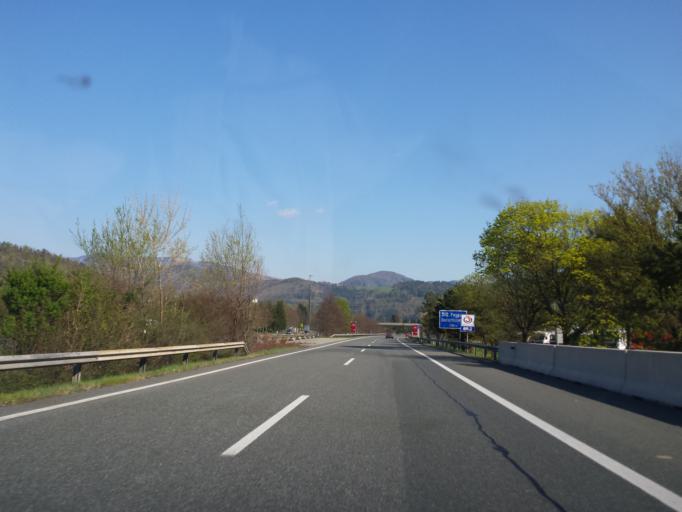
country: AT
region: Styria
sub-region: Politischer Bezirk Graz-Umgebung
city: Deutschfeistritz
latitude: 47.2060
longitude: 15.3158
